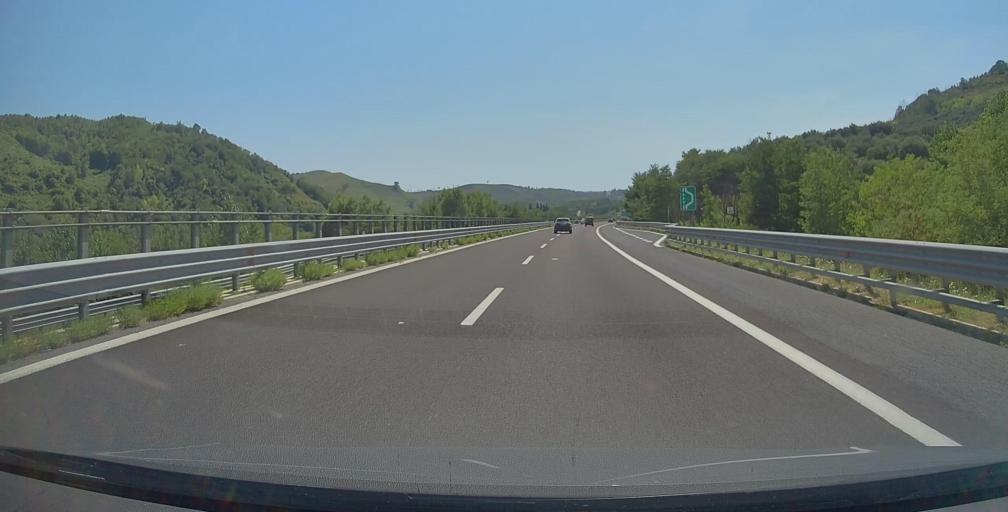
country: IT
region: Calabria
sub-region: Provincia di Vibo-Valentia
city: Francica
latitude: 38.5819
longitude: 16.1310
